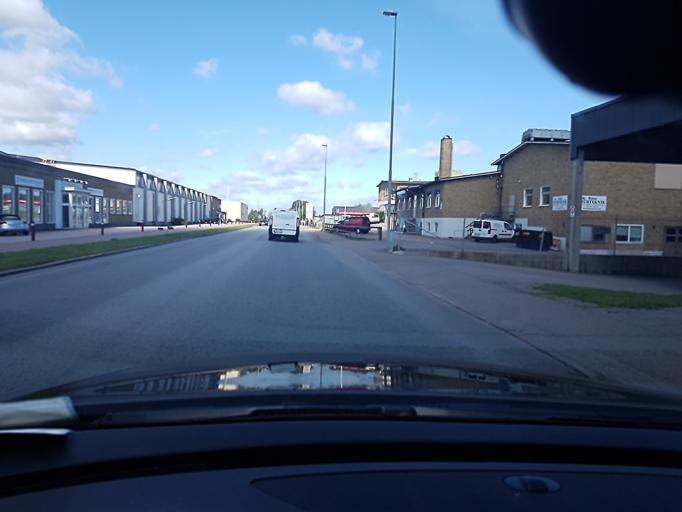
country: SE
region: Kalmar
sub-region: Kalmar Kommun
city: Kalmar
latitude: 56.6673
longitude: 16.3387
